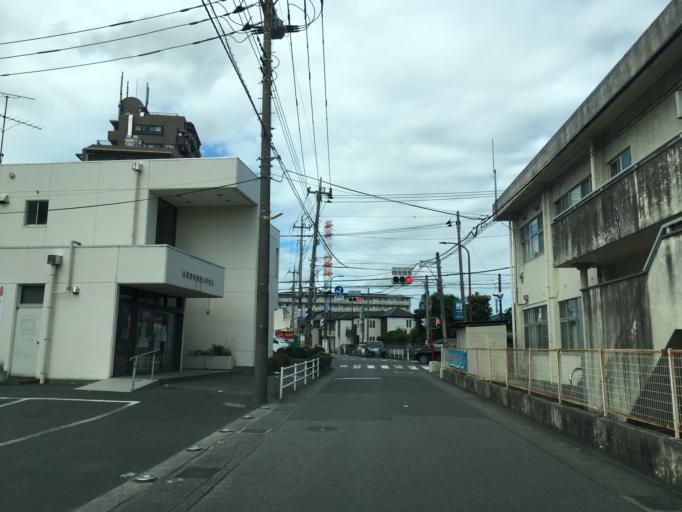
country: JP
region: Tokyo
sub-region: Machida-shi
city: Machida
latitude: 35.5528
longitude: 139.4216
